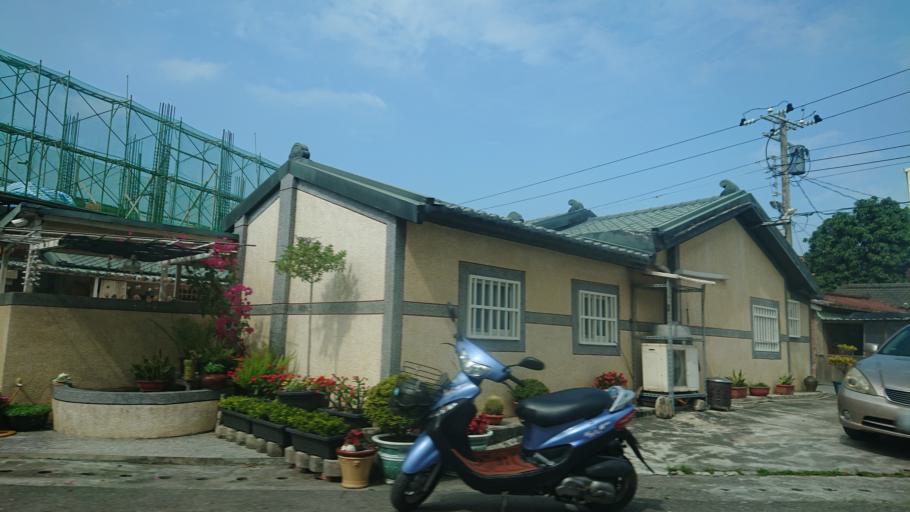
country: TW
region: Taiwan
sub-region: Chiayi
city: Taibao
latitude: 23.4699
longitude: 120.2436
